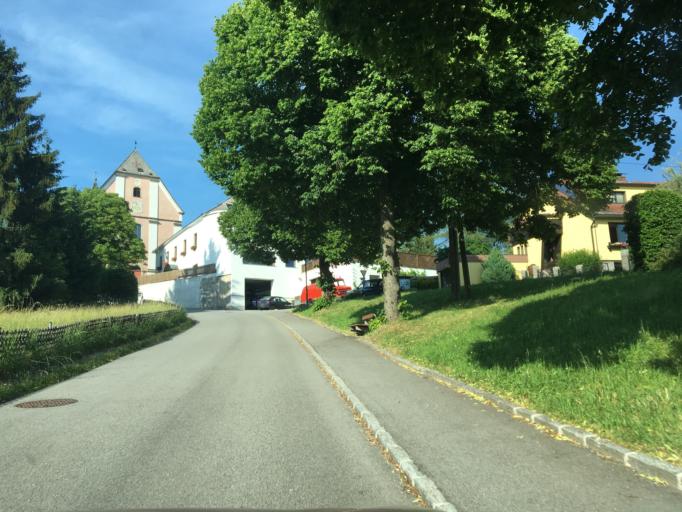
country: AT
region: Upper Austria
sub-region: Politischer Bezirk Urfahr-Umgebung
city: Bad Leonfelden
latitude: 48.5205
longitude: 14.2880
